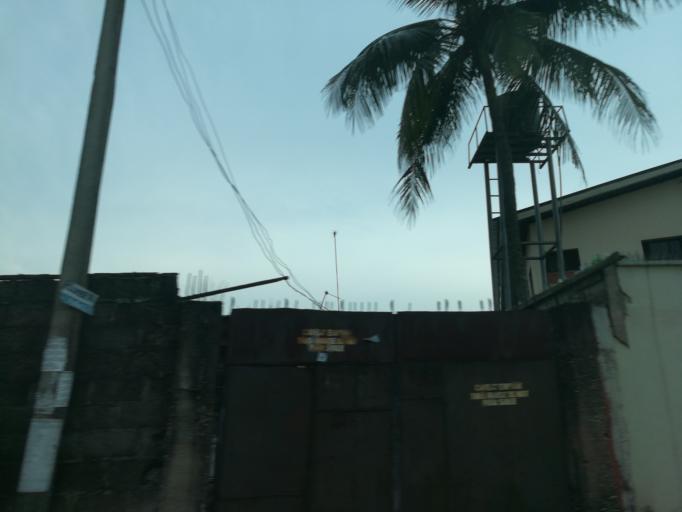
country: NG
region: Rivers
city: Port Harcourt
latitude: 4.8251
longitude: 7.0276
